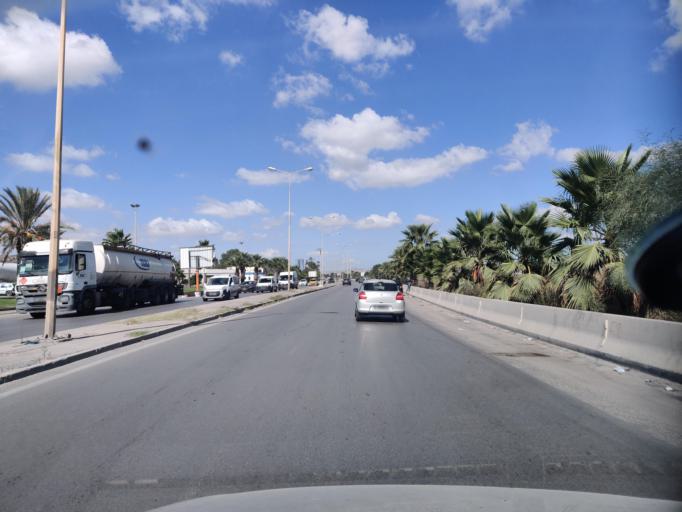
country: TN
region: Bin 'Arus
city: Ben Arous
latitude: 36.7787
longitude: 10.2052
